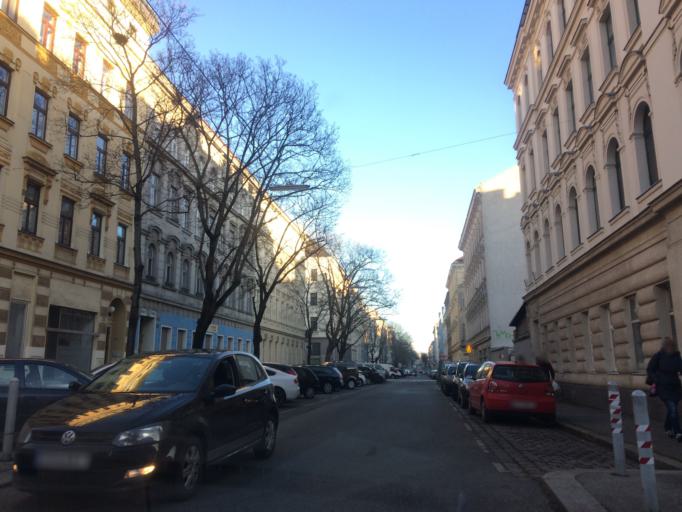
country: AT
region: Vienna
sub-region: Wien Stadt
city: Vienna
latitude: 48.1983
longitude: 16.3101
